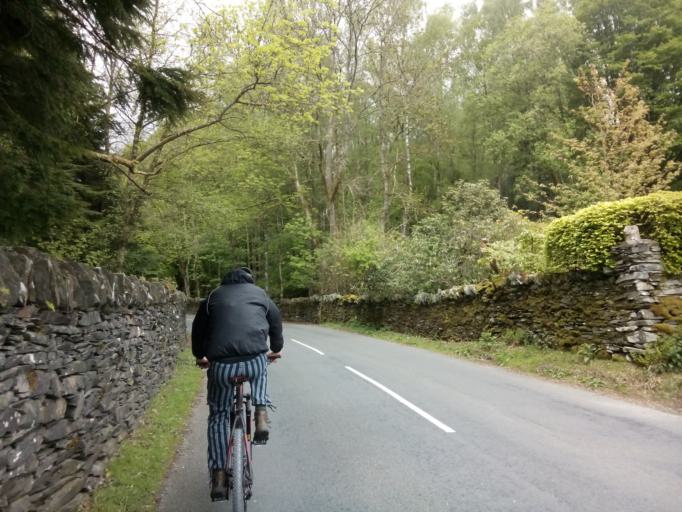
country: GB
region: England
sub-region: Cumbria
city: Ambleside
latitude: 54.4367
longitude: -3.0368
